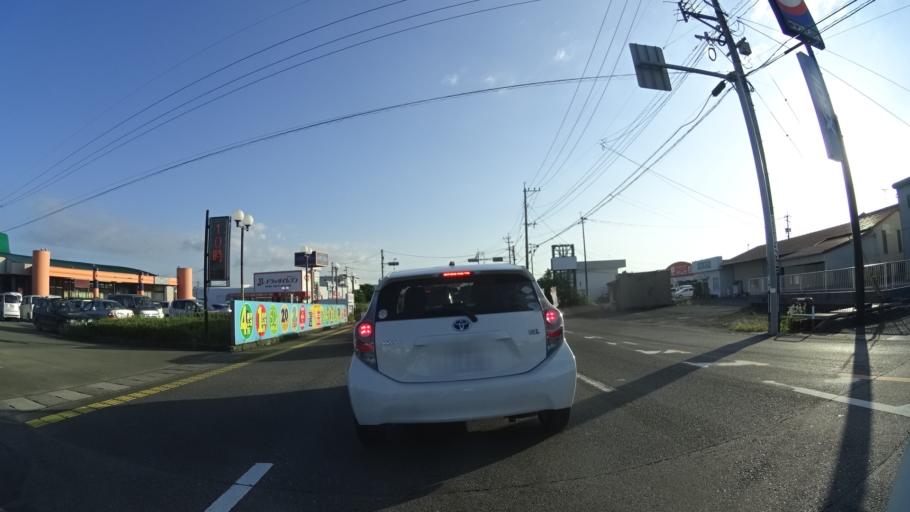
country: JP
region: Kumamoto
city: Matsubase
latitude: 32.6473
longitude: 130.6768
